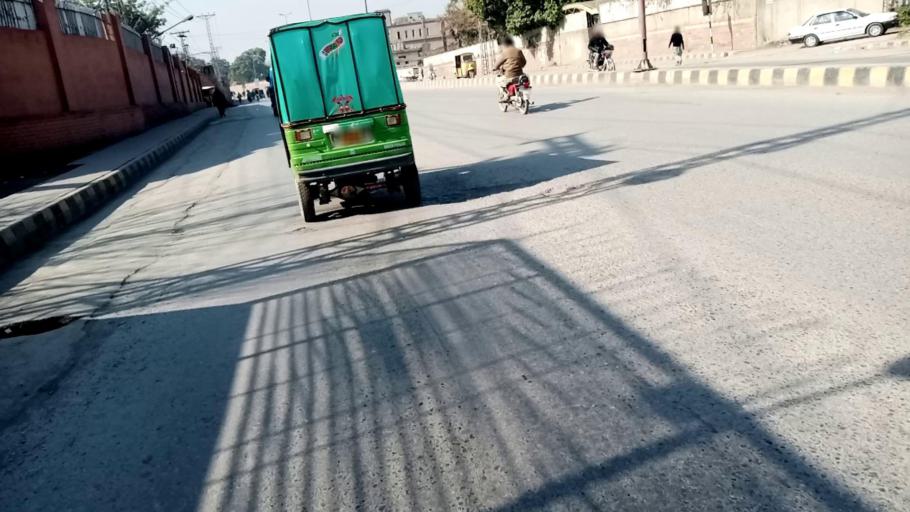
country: PK
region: Khyber Pakhtunkhwa
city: Peshawar
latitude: 34.0094
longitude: 71.5604
